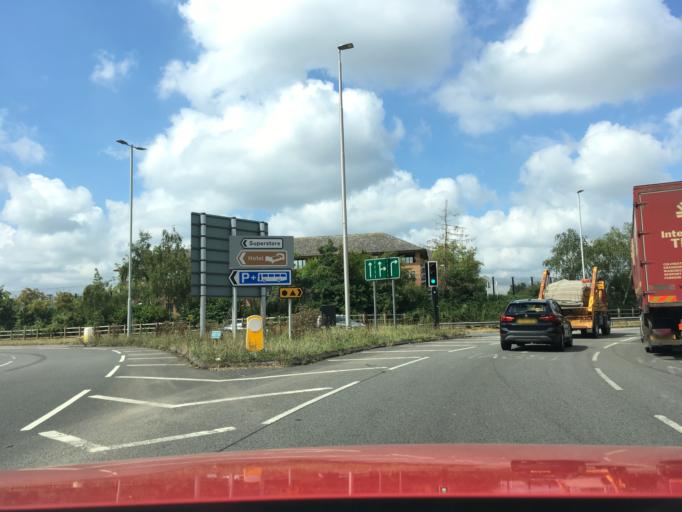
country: GB
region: England
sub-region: Gloucestershire
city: Barnwood
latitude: 51.8652
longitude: -2.1965
